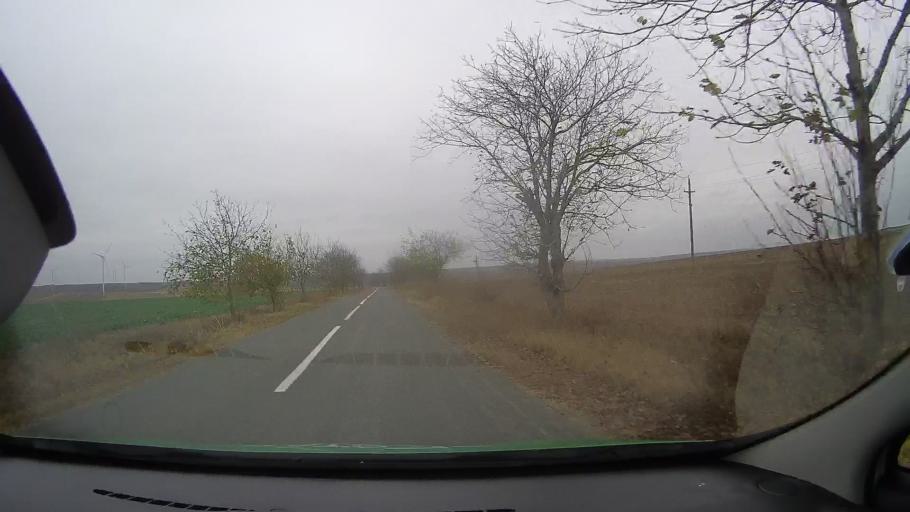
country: RO
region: Constanta
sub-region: Comuna Targusor
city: Targusor
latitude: 44.4816
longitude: 28.3718
